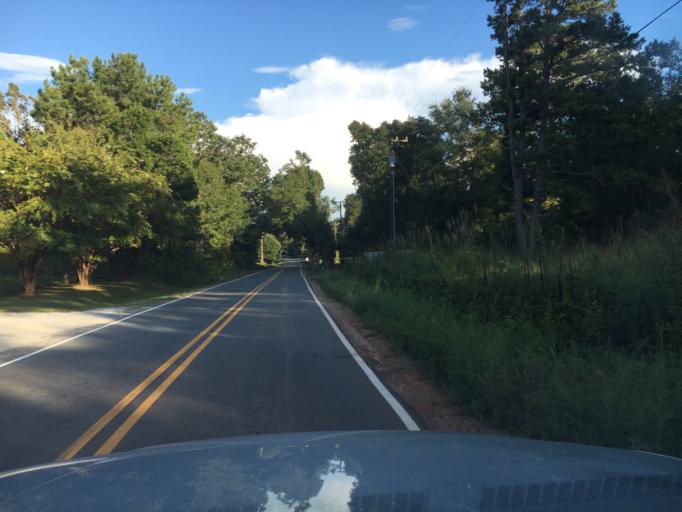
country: US
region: South Carolina
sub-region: Spartanburg County
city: Fairforest
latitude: 34.8996
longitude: -82.0350
